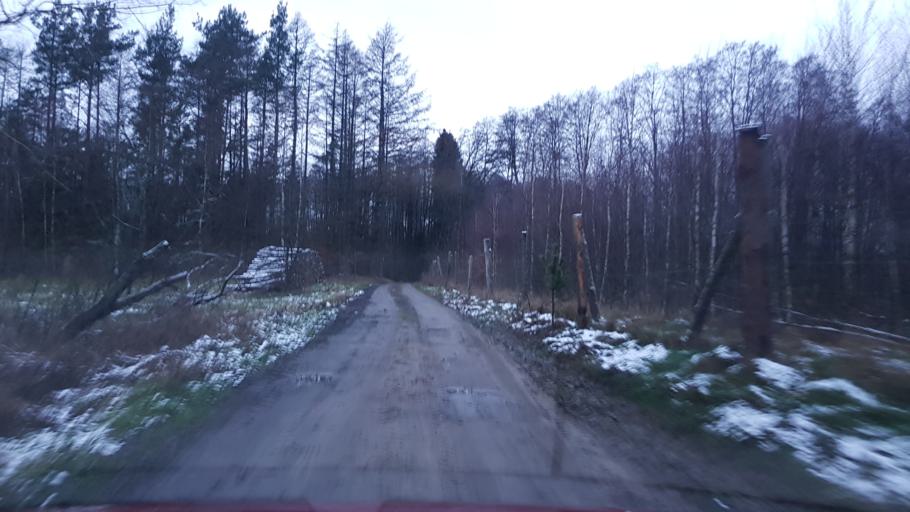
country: PL
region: Pomeranian Voivodeship
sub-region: Powiat bytowski
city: Tuchomie
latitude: 54.1458
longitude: 17.2999
